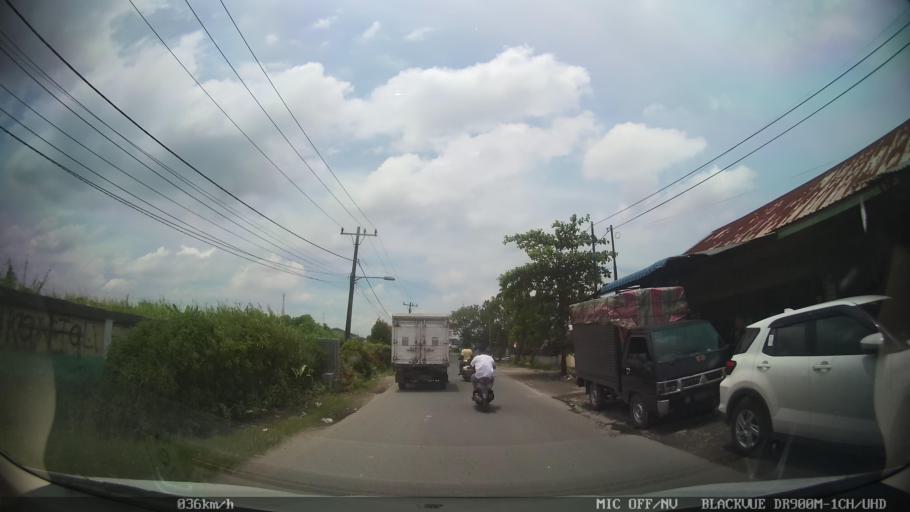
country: ID
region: North Sumatra
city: Labuhan Deli
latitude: 3.6816
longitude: 98.6696
